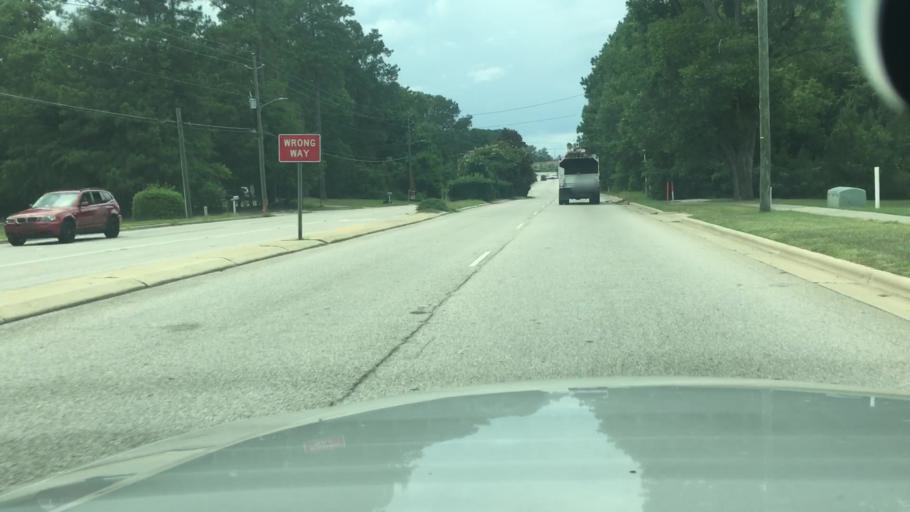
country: US
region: North Carolina
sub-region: Cumberland County
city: Fayetteville
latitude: 34.9989
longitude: -78.8961
